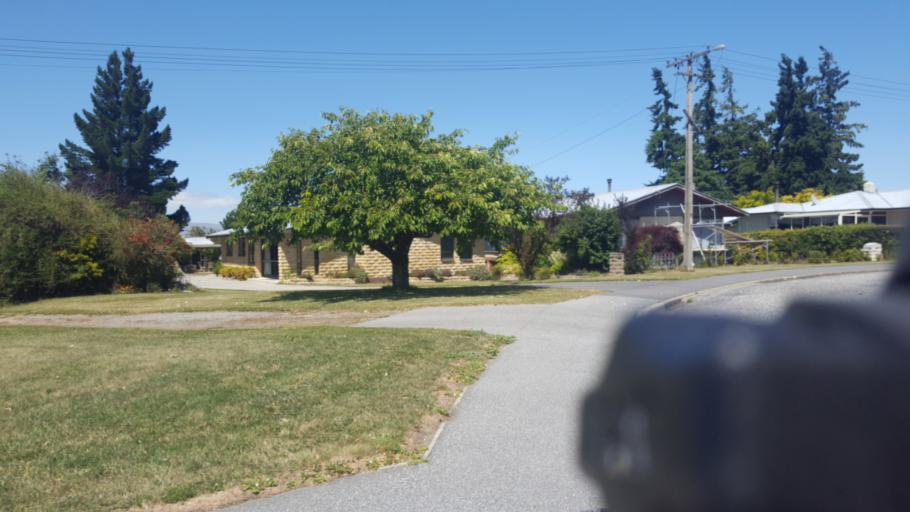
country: NZ
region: Otago
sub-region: Dunedin City
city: Dunedin
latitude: -45.1283
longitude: 170.1092
